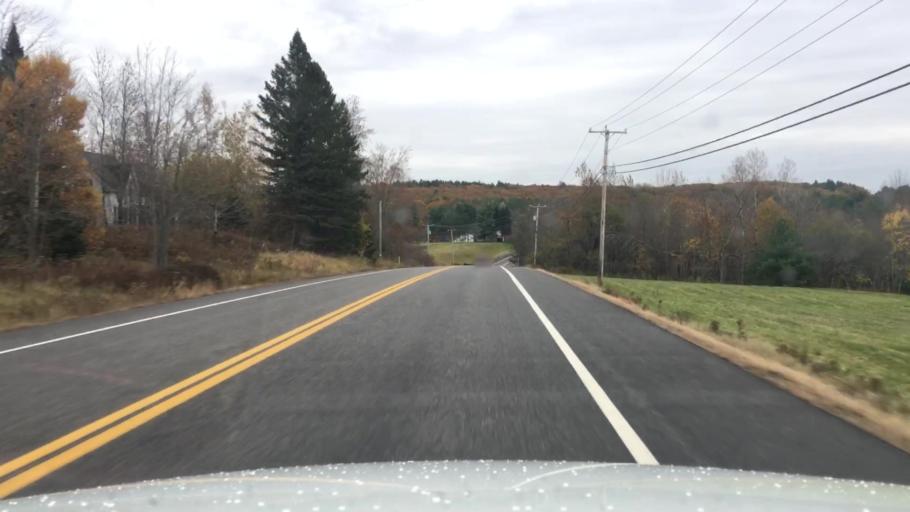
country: US
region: Maine
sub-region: Kennebec County
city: Pittston
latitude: 44.1917
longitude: -69.7478
